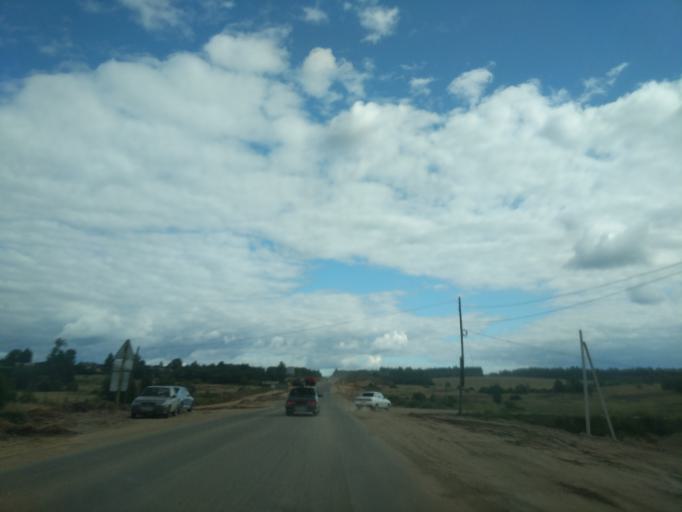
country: RU
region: Kostroma
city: Sudislavl'
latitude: 57.8763
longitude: 41.7307
